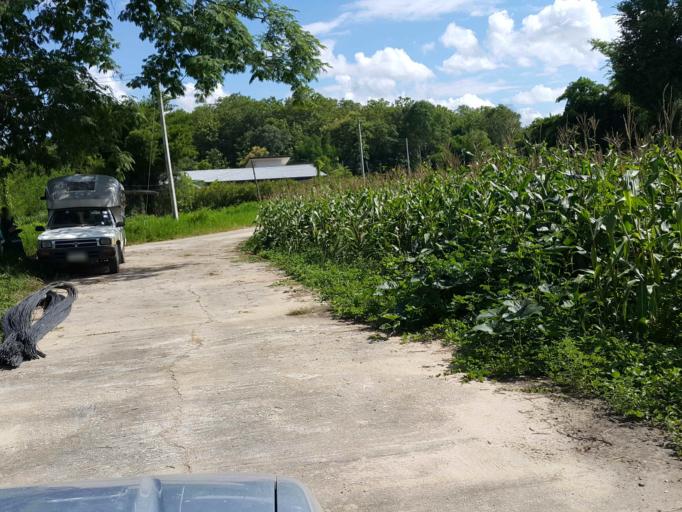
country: TH
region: Chiang Mai
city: Mae Taeng
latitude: 18.9689
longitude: 98.9102
